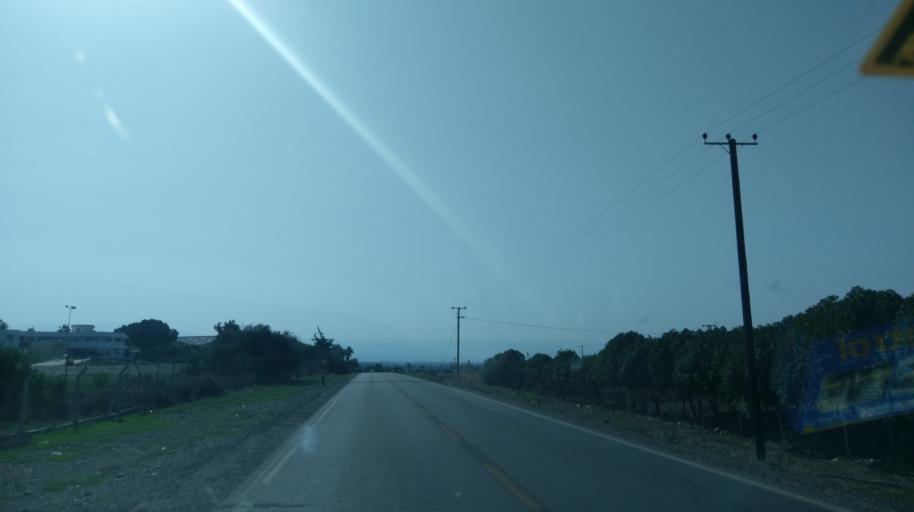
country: CY
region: Lefkosia
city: Morfou
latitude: 35.2311
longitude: 33.0163
